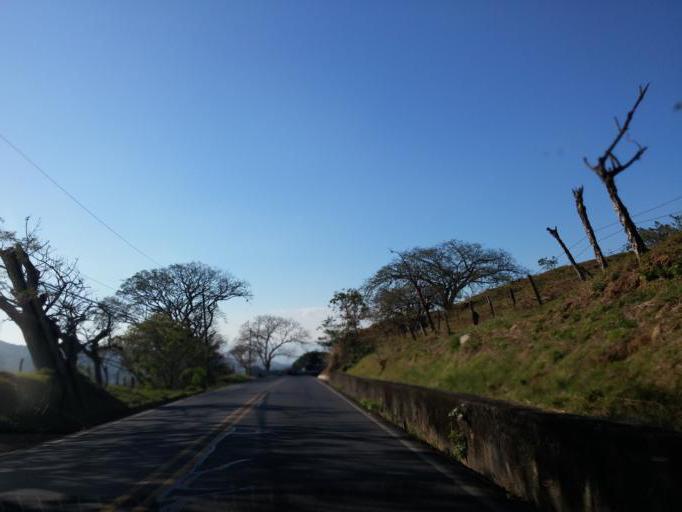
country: CR
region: Heredia
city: Colon
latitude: 9.8916
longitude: -84.2284
